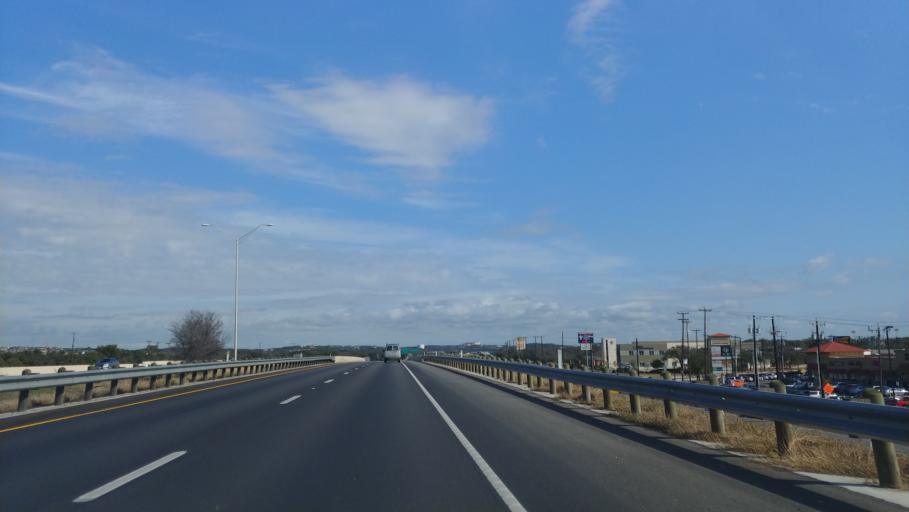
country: US
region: Texas
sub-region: Bexar County
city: Helotes
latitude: 29.5687
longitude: -98.6521
